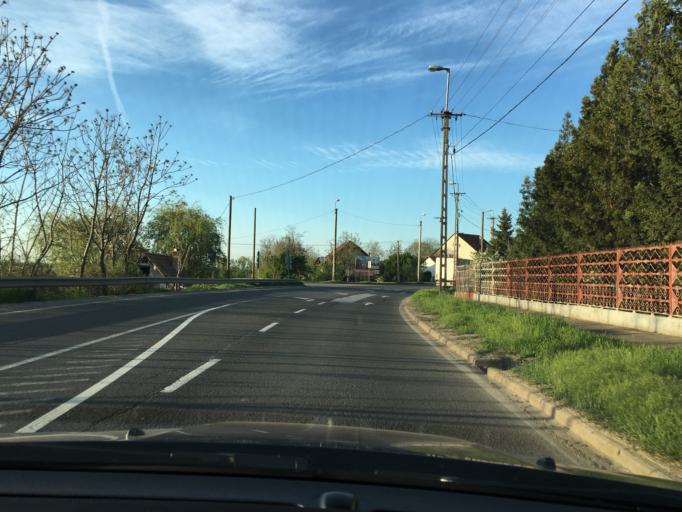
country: HU
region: Hajdu-Bihar
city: Mikepercs
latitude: 47.4360
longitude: 21.6284
